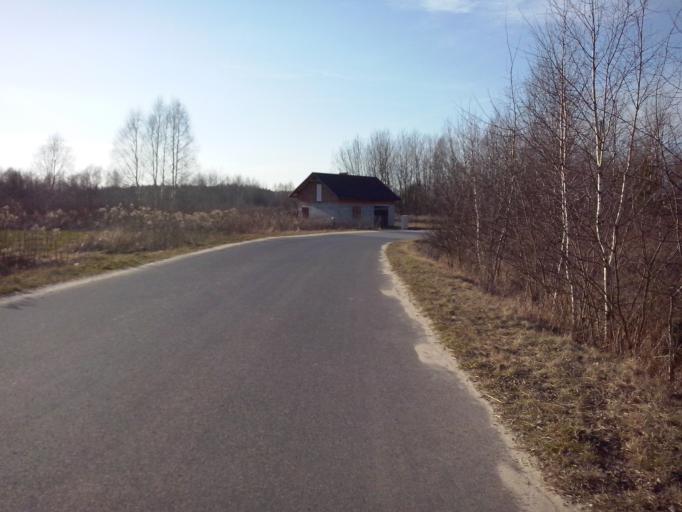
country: PL
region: Subcarpathian Voivodeship
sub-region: Powiat nizanski
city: Krzeszow
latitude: 50.4122
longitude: 22.3518
